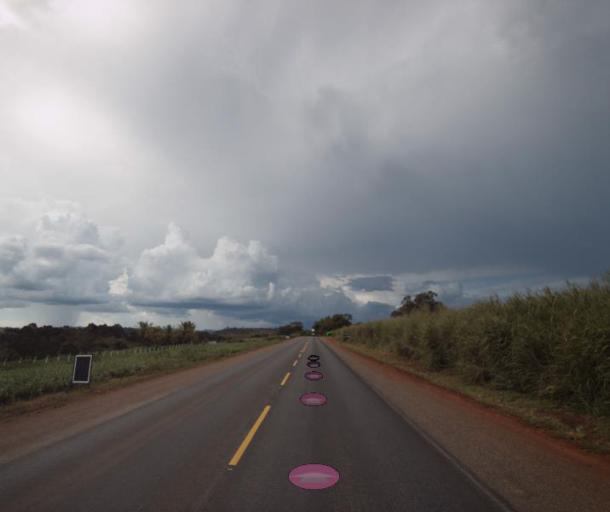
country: BR
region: Goias
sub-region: Ceres
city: Ceres
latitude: -15.2101
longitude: -49.5472
